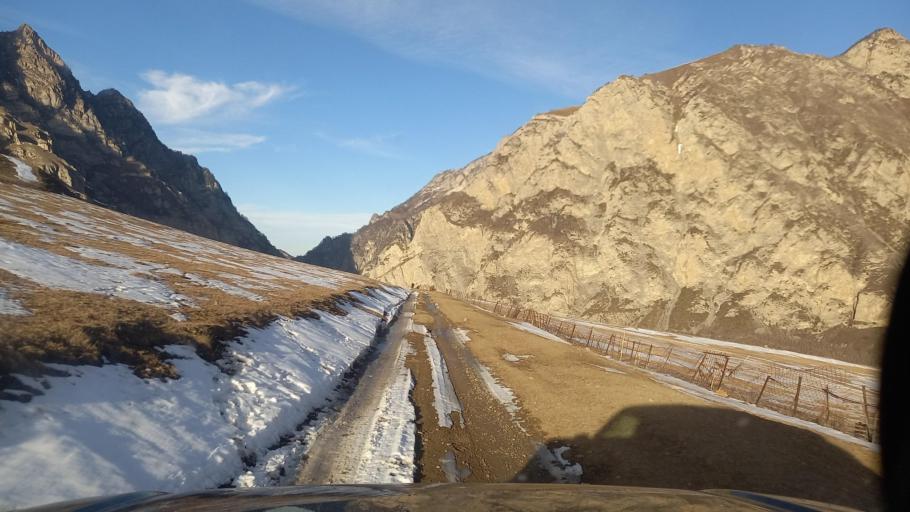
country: RU
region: Ingushetiya
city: Dzhayrakh
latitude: 42.8528
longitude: 44.5149
